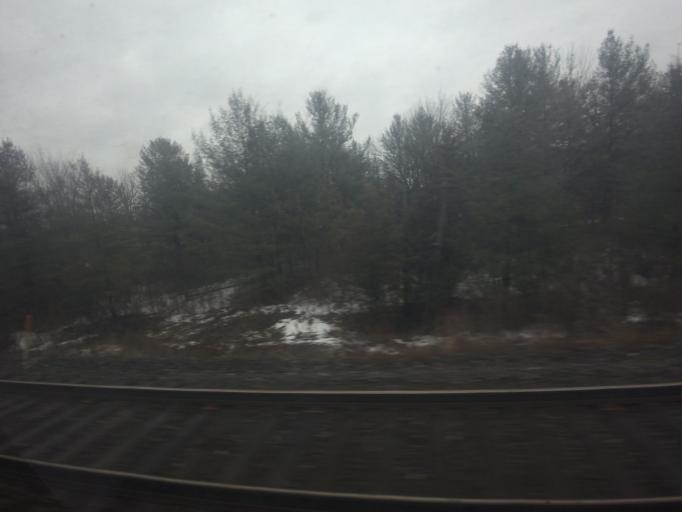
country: CA
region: Ontario
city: Kingston
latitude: 44.2381
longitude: -76.6240
